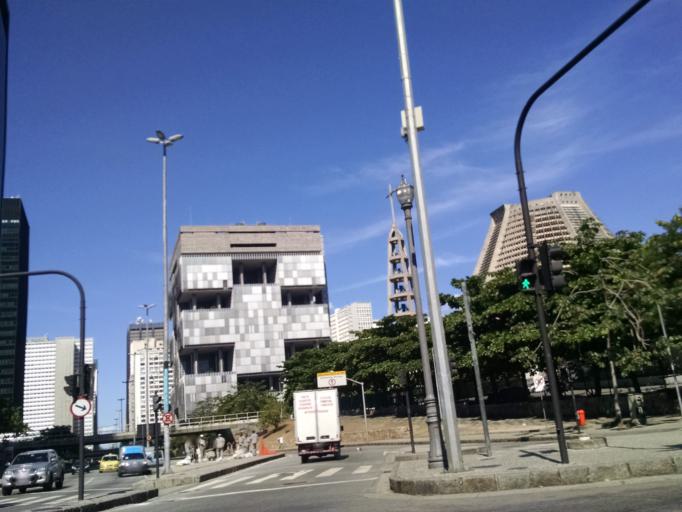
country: BR
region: Rio de Janeiro
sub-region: Rio De Janeiro
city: Rio de Janeiro
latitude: -22.9101
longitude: -43.1832
